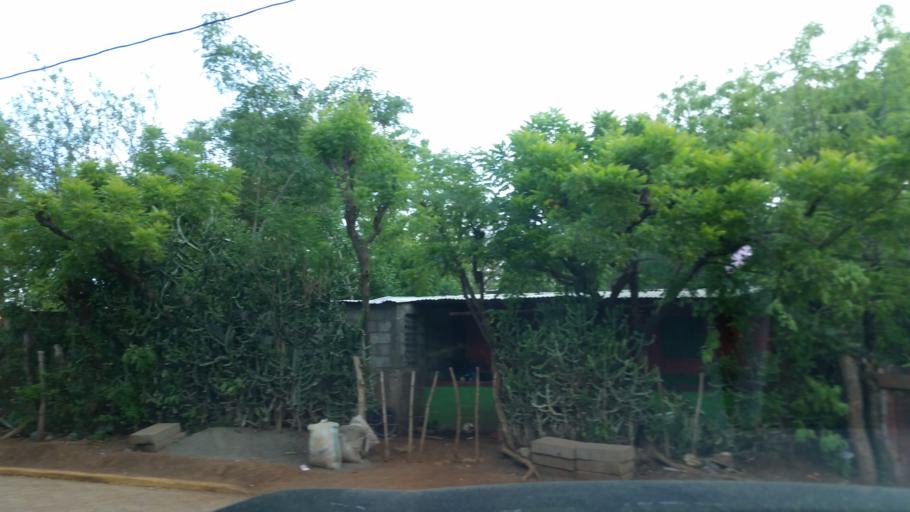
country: NI
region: Managua
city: Masachapa
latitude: 11.8131
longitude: -86.4880
